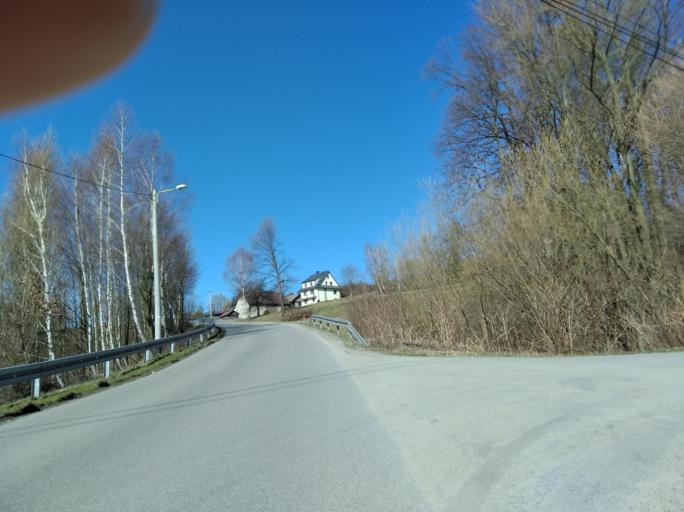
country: PL
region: Subcarpathian Voivodeship
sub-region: Powiat strzyzowski
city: Wisniowa
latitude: 49.8959
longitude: 21.6654
